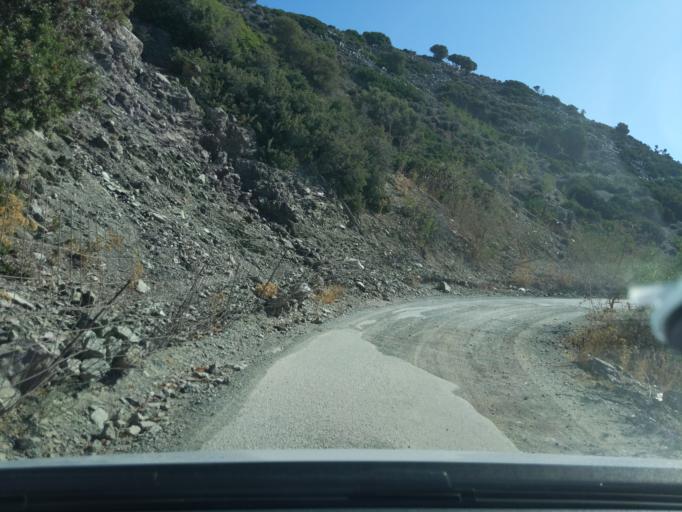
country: GR
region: Crete
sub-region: Nomos Irakleiou
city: Moires
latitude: 34.9396
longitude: 24.8164
